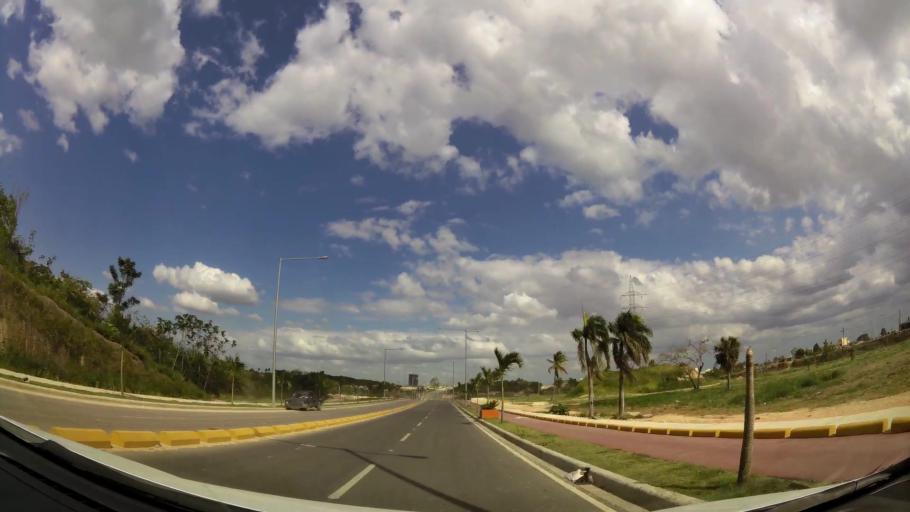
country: DO
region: Nacional
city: Ensanche Luperon
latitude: 18.5348
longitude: -69.8918
